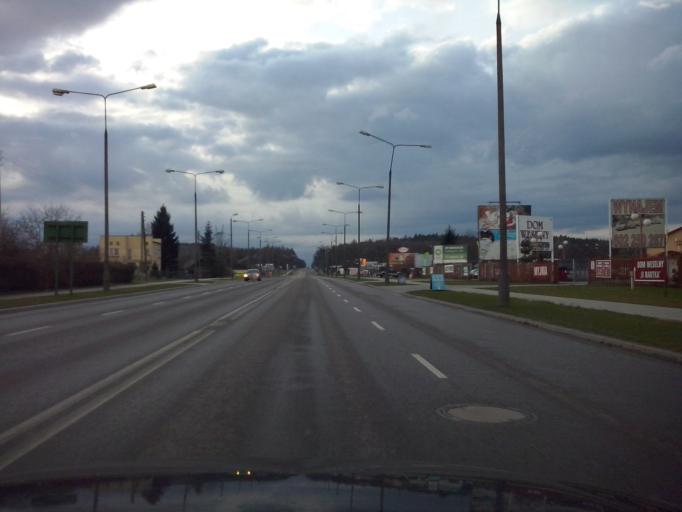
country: PL
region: Lublin Voivodeship
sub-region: Chelm
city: Chelm
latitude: 51.1474
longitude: 23.4333
